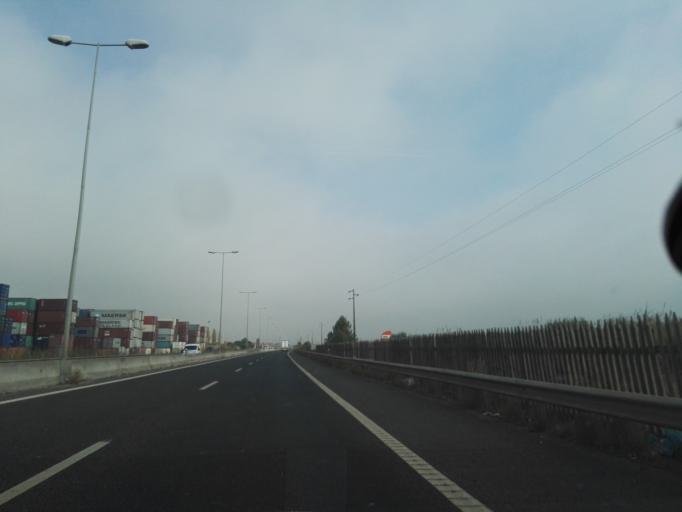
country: PT
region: Lisbon
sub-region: Loures
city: Bobadela
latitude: 38.8054
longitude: -9.0911
